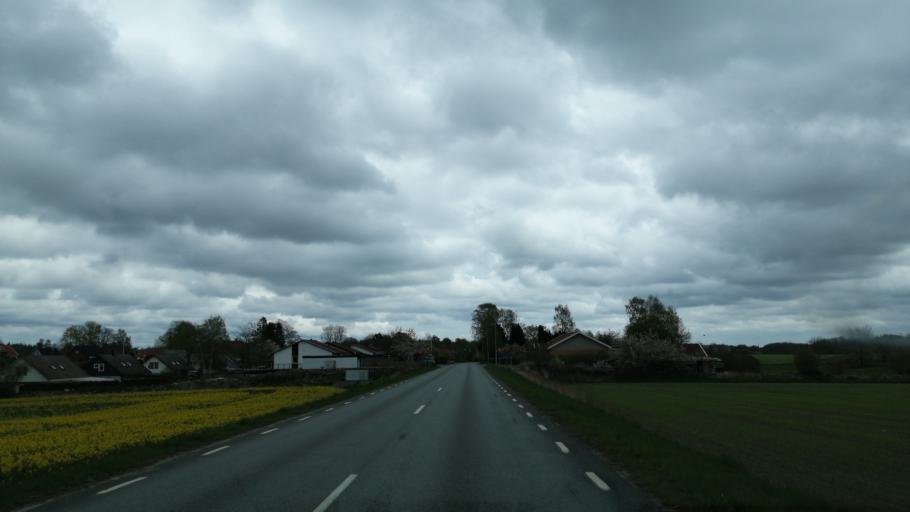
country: SE
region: Skane
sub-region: Kristianstads Kommun
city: Onnestad
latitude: 55.9931
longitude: 14.0292
